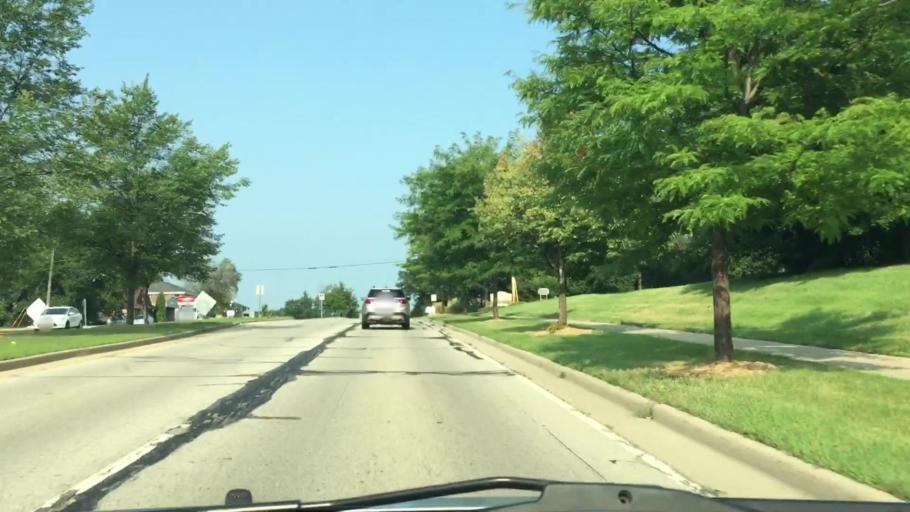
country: US
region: Wisconsin
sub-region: Waukesha County
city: New Berlin
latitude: 43.0169
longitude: -88.1199
